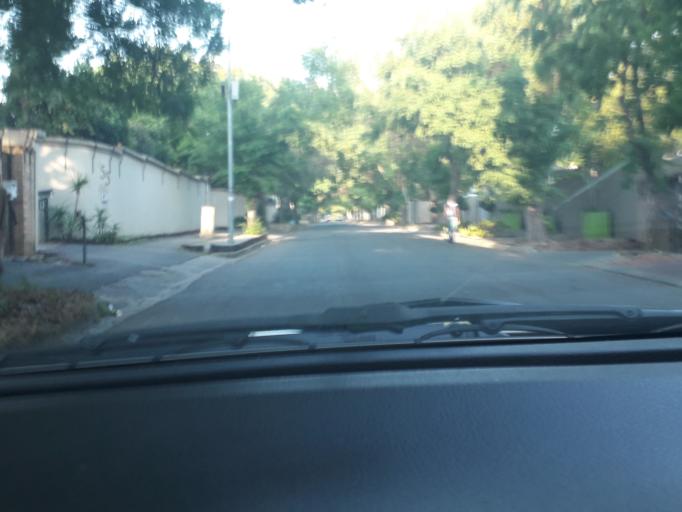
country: ZA
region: Gauteng
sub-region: City of Johannesburg Metropolitan Municipality
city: Johannesburg
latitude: -26.1258
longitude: 28.0788
